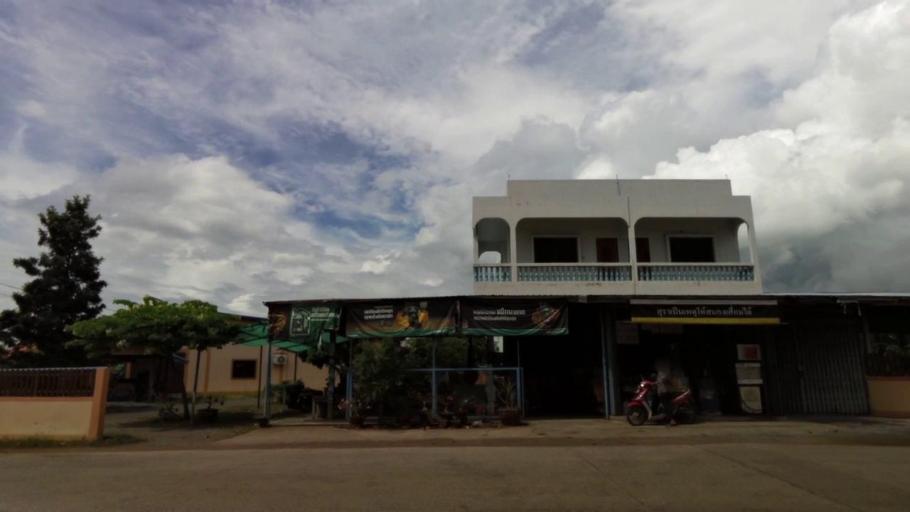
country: TH
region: Nakhon Sawan
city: Phai Sali
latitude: 15.6019
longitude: 100.6476
